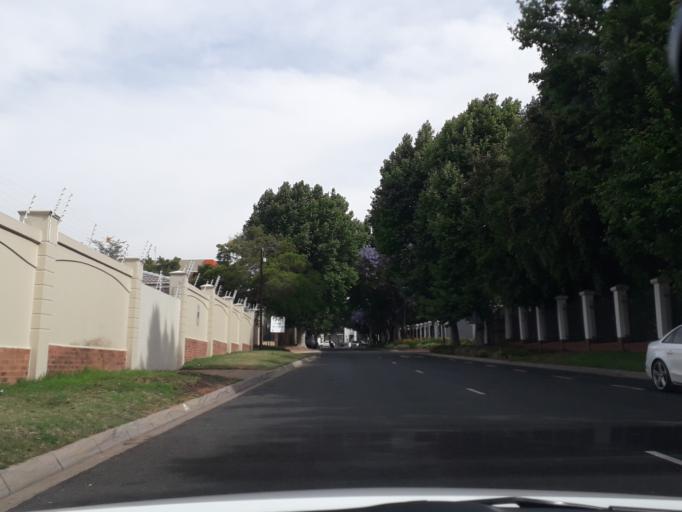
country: ZA
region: Gauteng
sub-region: City of Johannesburg Metropolitan Municipality
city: Diepsloot
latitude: -26.0453
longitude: 28.0212
